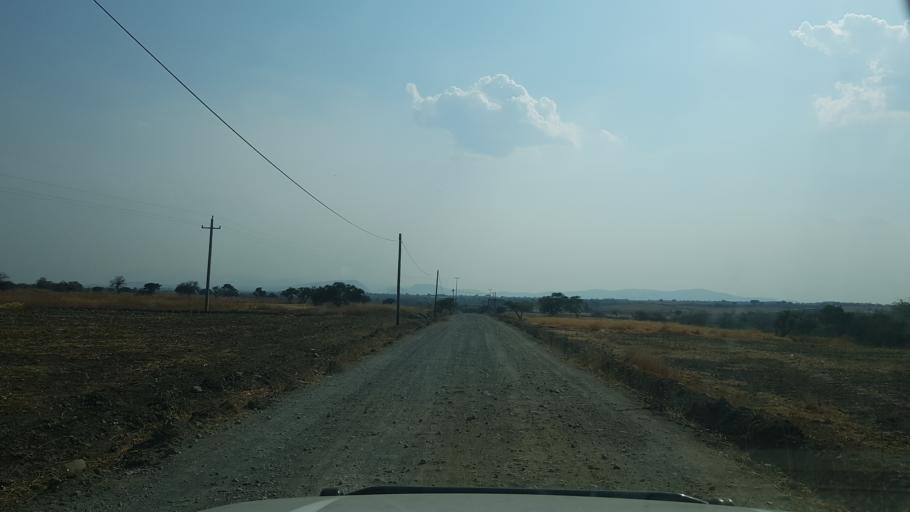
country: MX
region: Morelos
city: Tlacotepec
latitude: 18.7756
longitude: -98.7327
